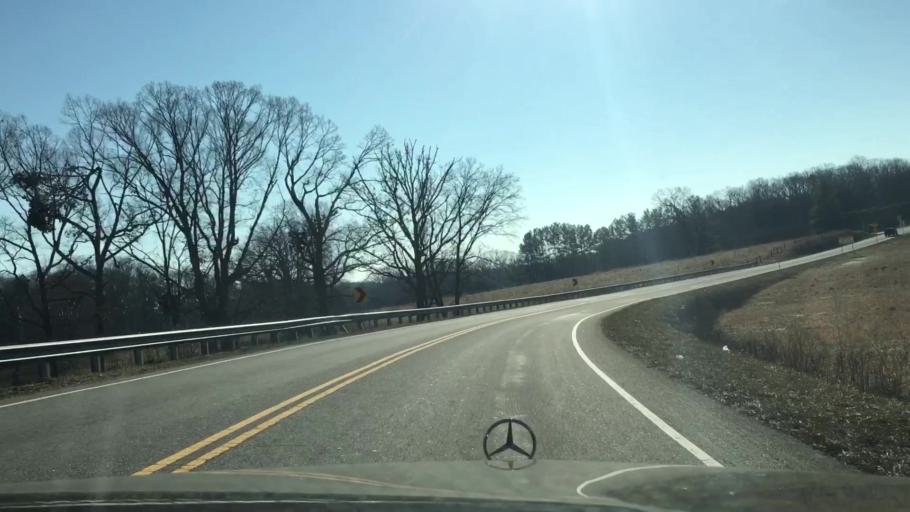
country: US
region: Virginia
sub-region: Campbell County
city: Altavista
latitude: 37.1458
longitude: -79.3102
